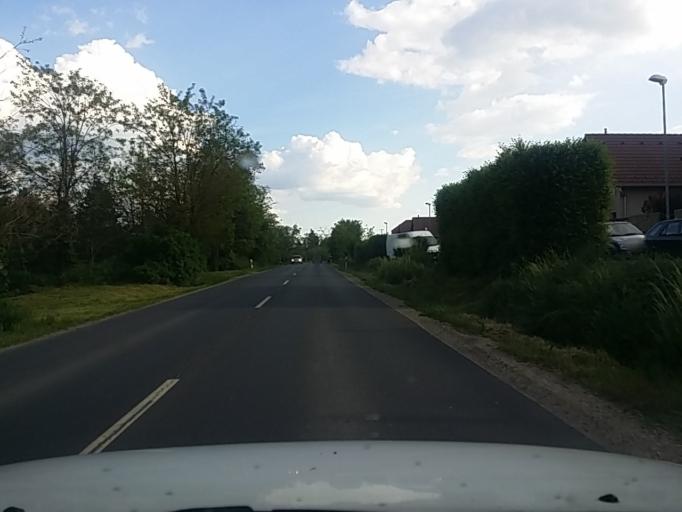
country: HU
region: Pest
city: Fot
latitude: 47.6228
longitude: 19.1986
